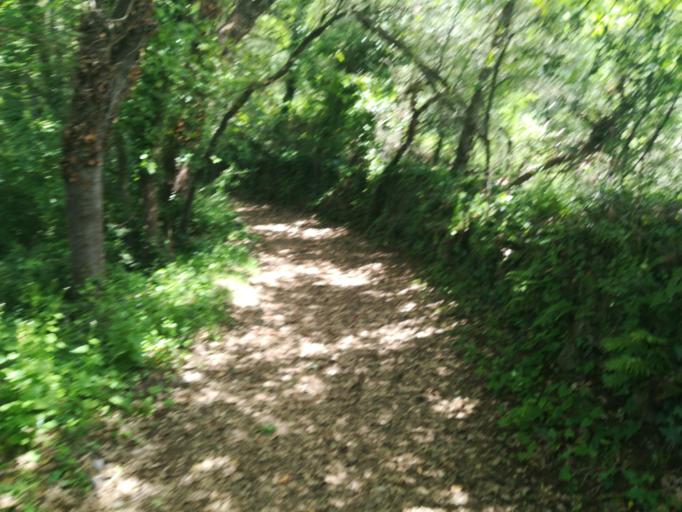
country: ES
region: Catalonia
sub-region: Provincia de Girona
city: Sant Cristofol de les Fonts
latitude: 42.1756
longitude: 2.4995
